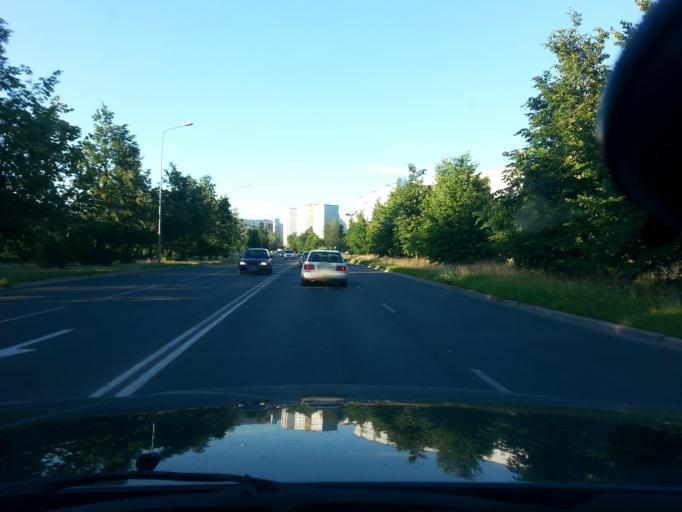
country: LV
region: Stopini
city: Ulbroka
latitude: 56.9601
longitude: 24.2299
